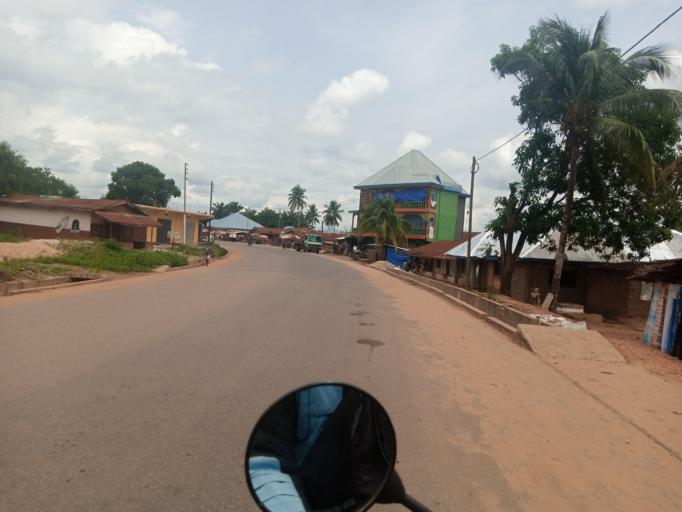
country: SL
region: Southern Province
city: Bo
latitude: 7.9524
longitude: -11.7536
